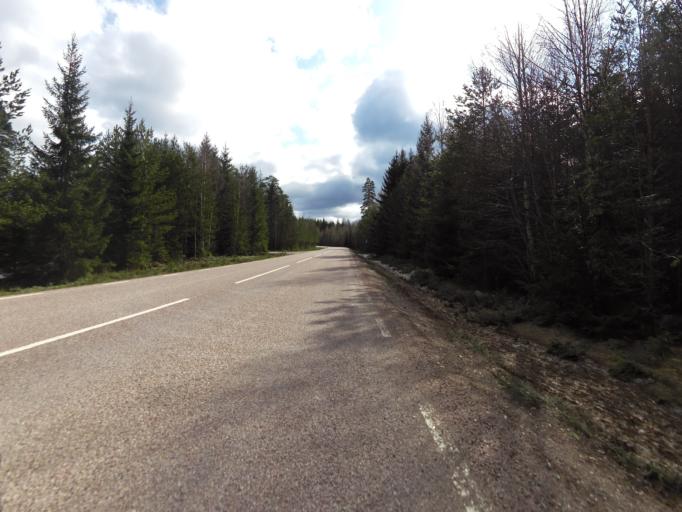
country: SE
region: Dalarna
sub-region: Avesta Kommun
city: Horndal
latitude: 60.3013
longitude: 16.2680
